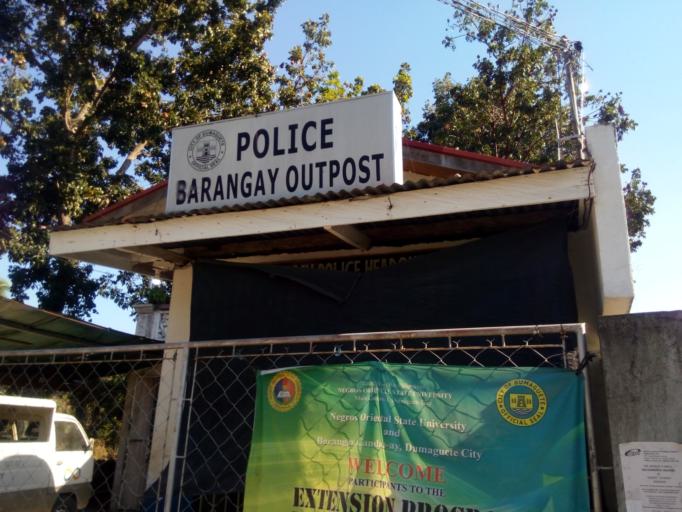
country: PH
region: Central Visayas
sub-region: Province of Negros Oriental
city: Valencia
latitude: 9.3135
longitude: 123.2592
